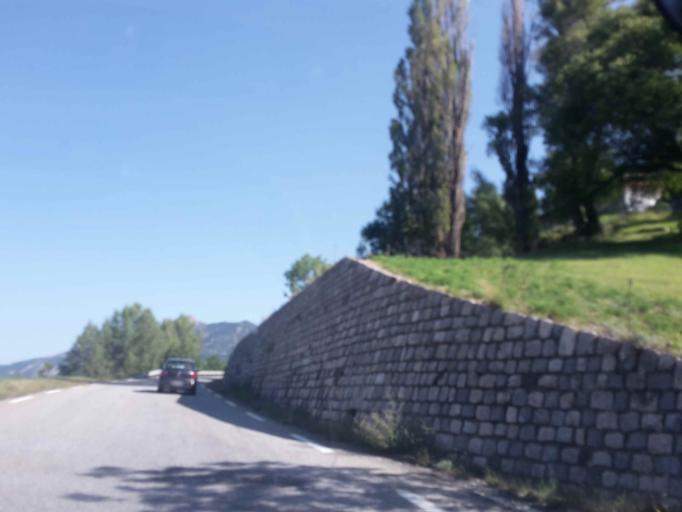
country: FR
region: Provence-Alpes-Cote d'Azur
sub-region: Departement des Hautes-Alpes
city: Guillestre
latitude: 44.6374
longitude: 6.6662
